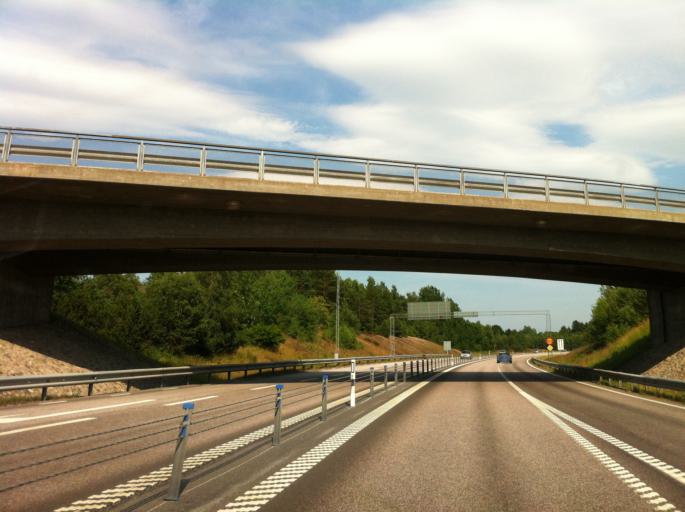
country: SE
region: Kalmar
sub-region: Kalmar Kommun
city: Trekanten
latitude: 56.6880
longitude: 16.1212
